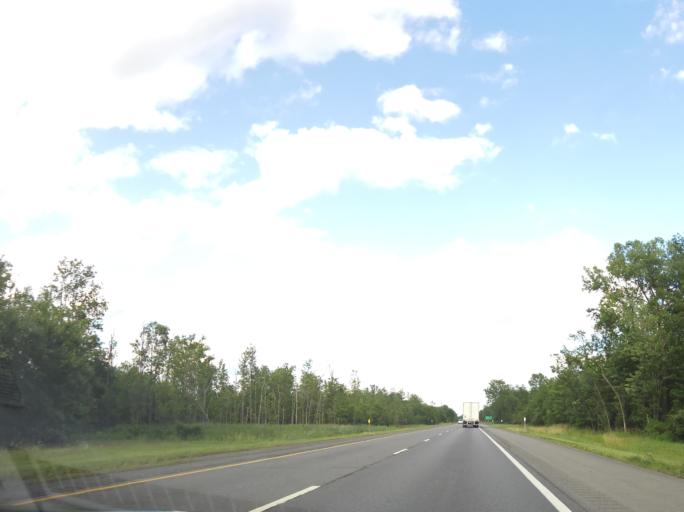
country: US
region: New York
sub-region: Erie County
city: Akron
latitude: 43.0094
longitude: -78.3860
